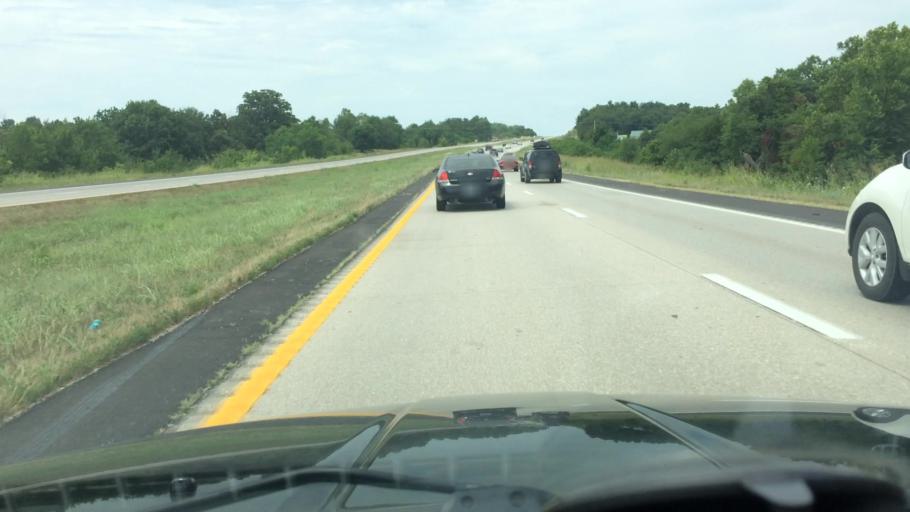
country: US
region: Missouri
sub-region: Greene County
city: Willard
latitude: 37.4329
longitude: -93.3554
